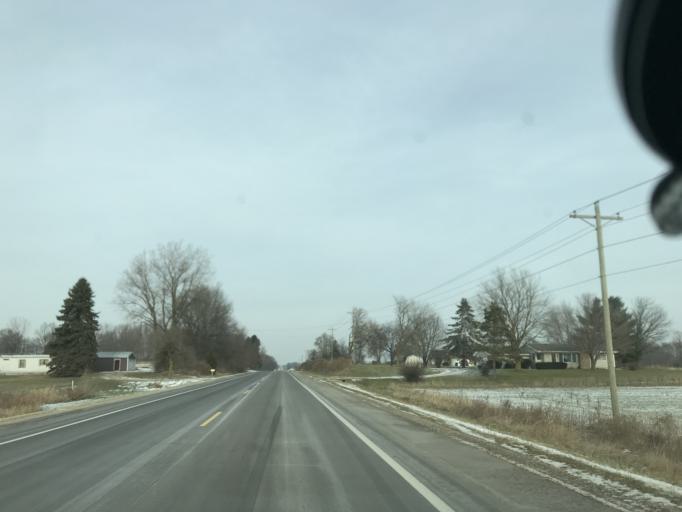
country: US
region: Michigan
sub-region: Ionia County
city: Lake Odessa
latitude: 42.7896
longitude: -85.0744
